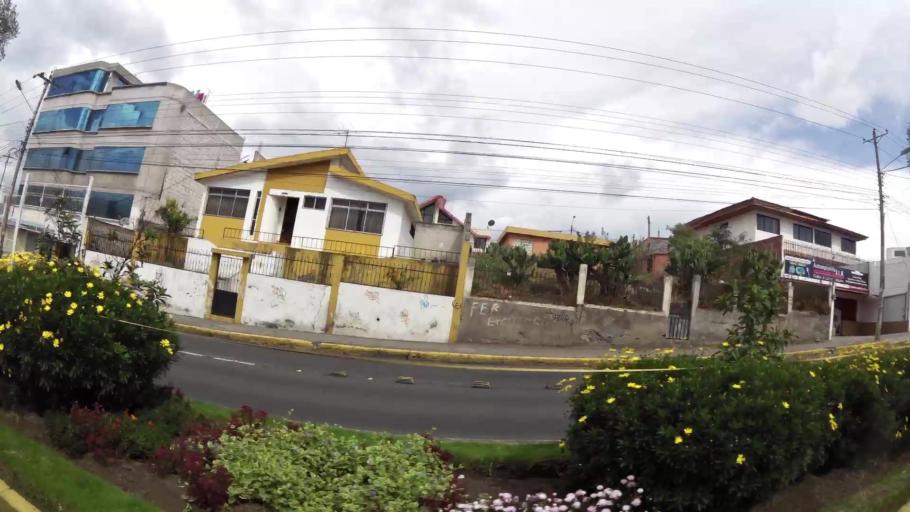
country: EC
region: Tungurahua
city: Ambato
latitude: -1.2704
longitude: -78.6293
